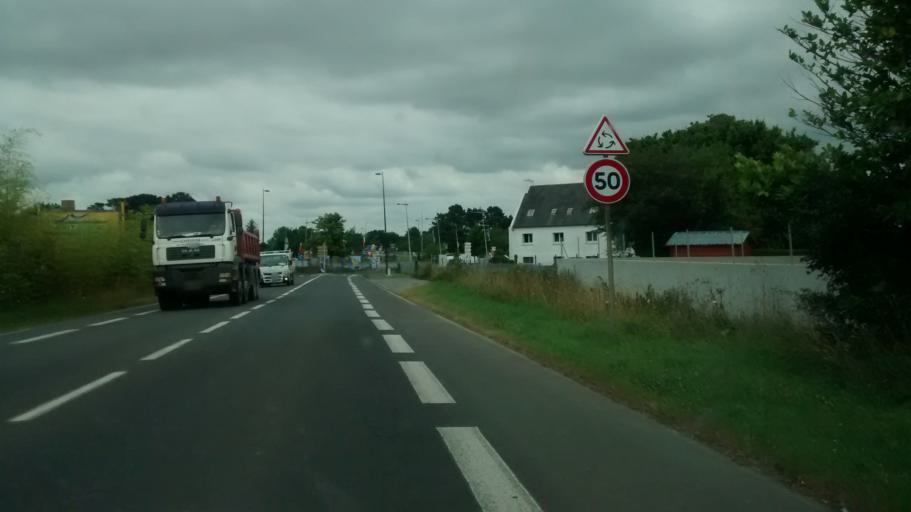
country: FR
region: Brittany
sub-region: Departement du Finistere
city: Plougastel-Daoulas
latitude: 48.3808
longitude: -4.3785
